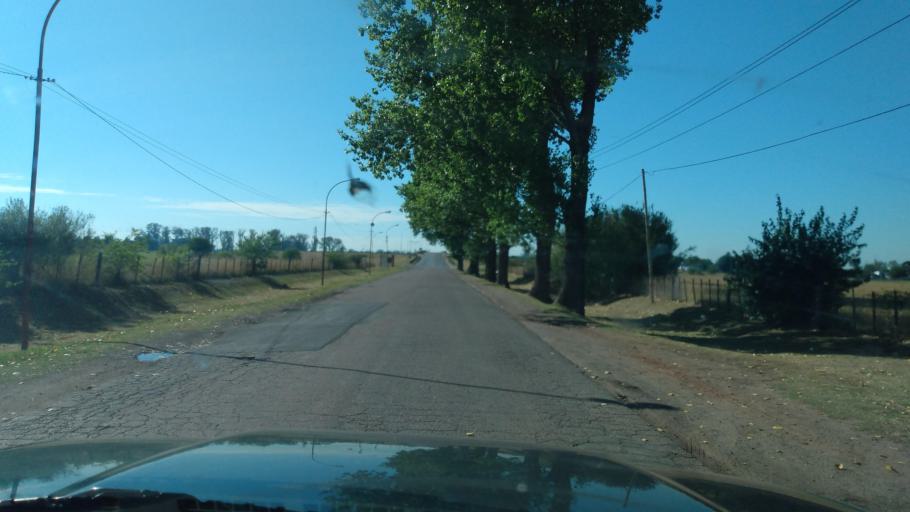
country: AR
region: Buenos Aires
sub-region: Partido de Lujan
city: Lujan
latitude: -34.6046
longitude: -59.1744
